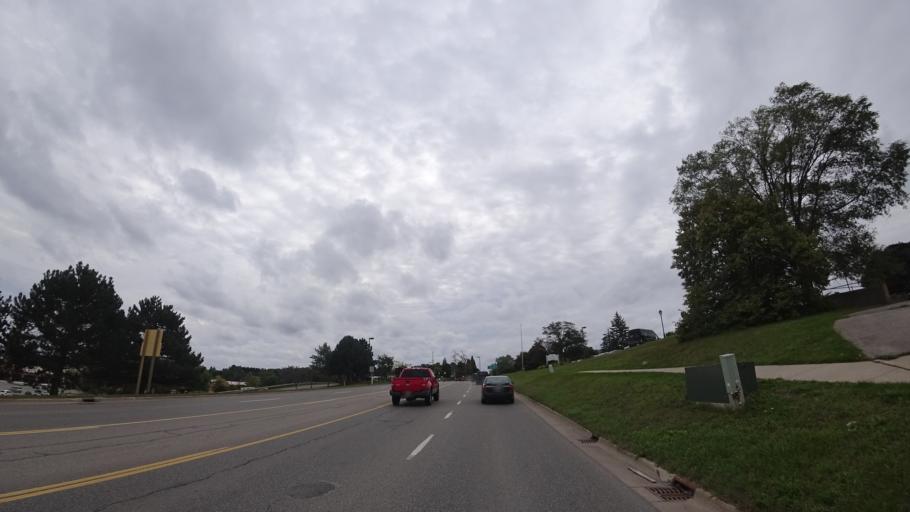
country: US
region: Michigan
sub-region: Emmet County
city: Petoskey
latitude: 45.3621
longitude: -84.9710
